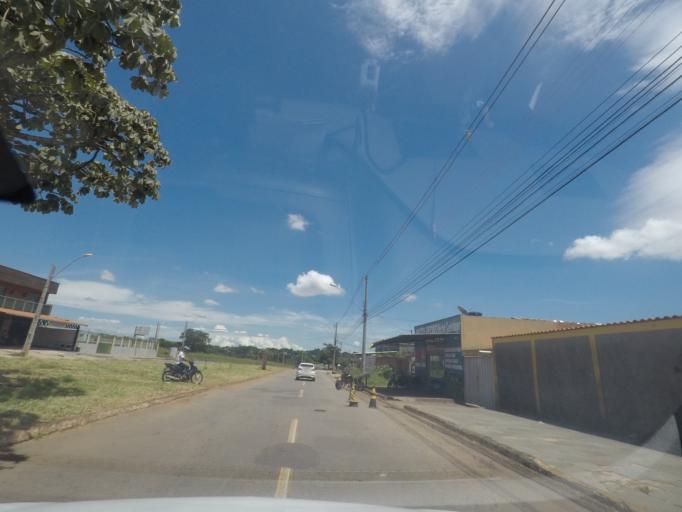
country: BR
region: Goias
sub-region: Goiania
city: Goiania
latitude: -16.7328
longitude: -49.3641
